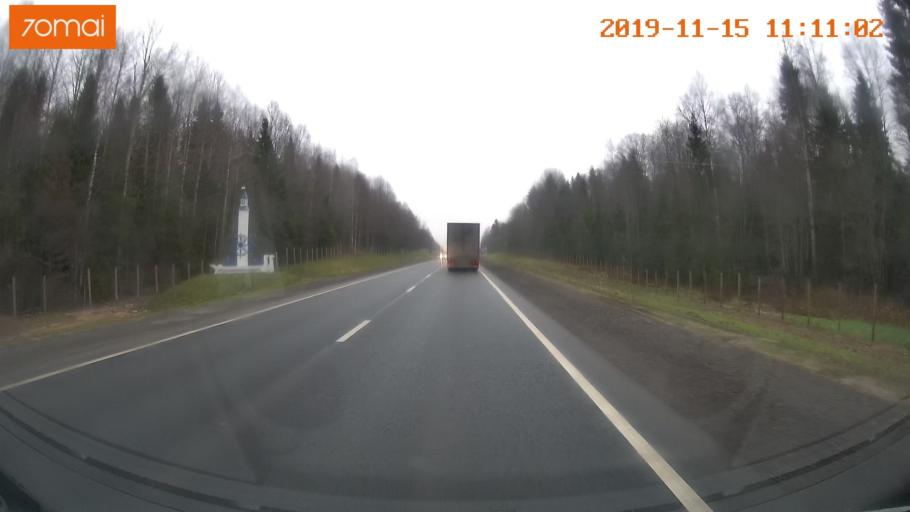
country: RU
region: Vologda
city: Chebsara
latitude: 59.1212
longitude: 39.1337
